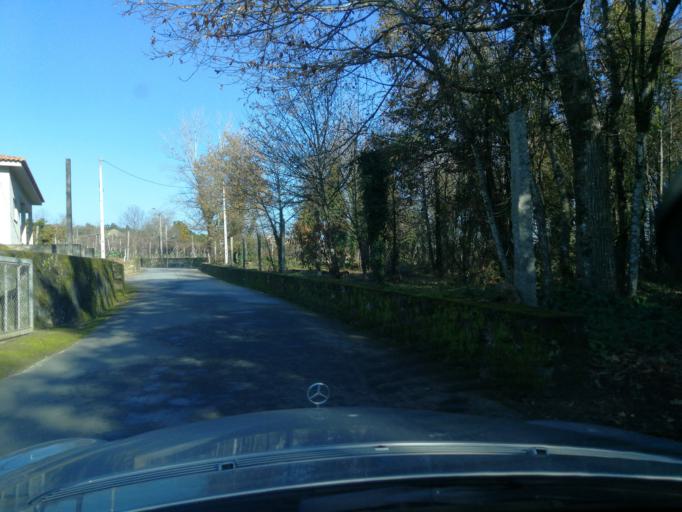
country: PT
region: Braga
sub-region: Braga
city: Adaufe
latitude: 41.6104
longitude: -8.3993
